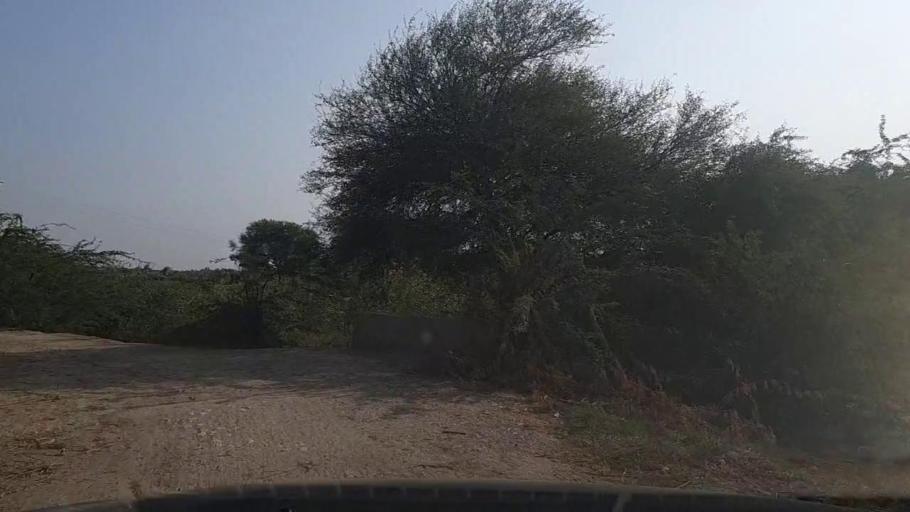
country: PK
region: Sindh
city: Mirpur Sakro
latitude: 24.6243
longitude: 67.7539
